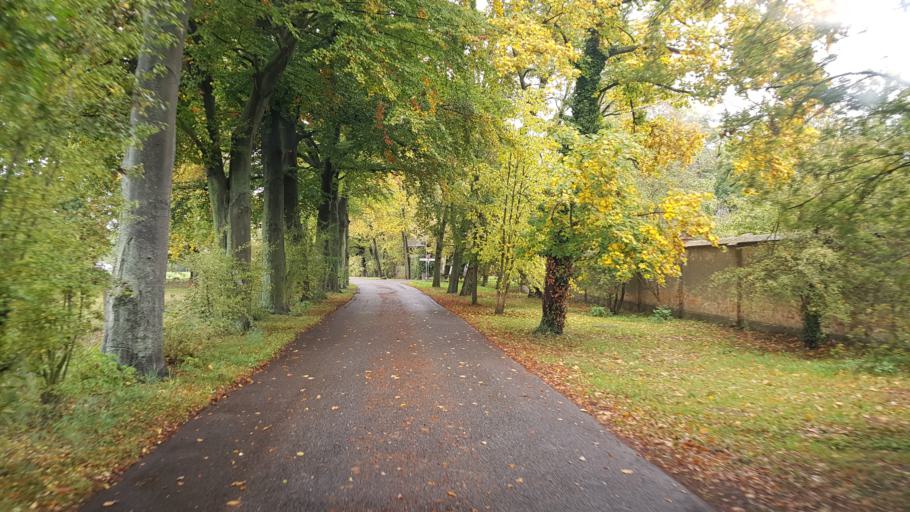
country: DE
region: Brandenburg
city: Altdobern
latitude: 51.6527
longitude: 14.0317
